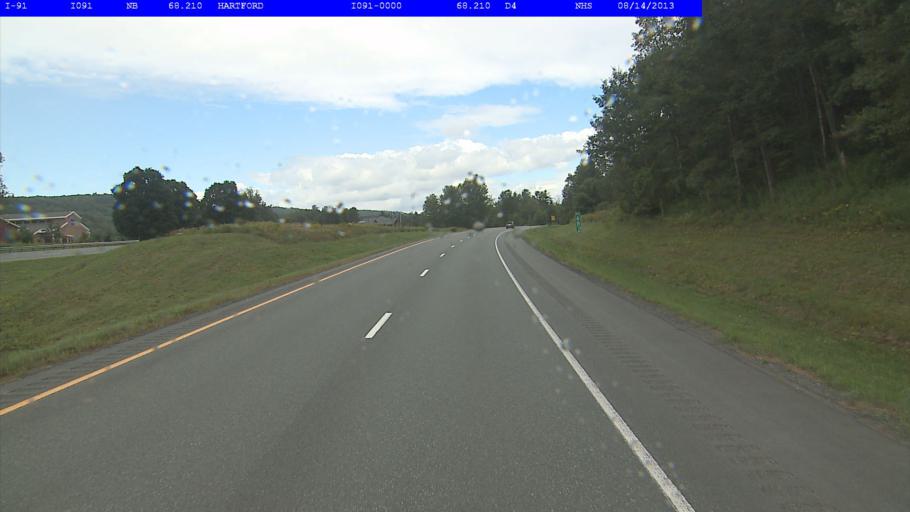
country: US
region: Vermont
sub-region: Windsor County
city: White River Junction
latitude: 43.6179
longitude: -72.3476
